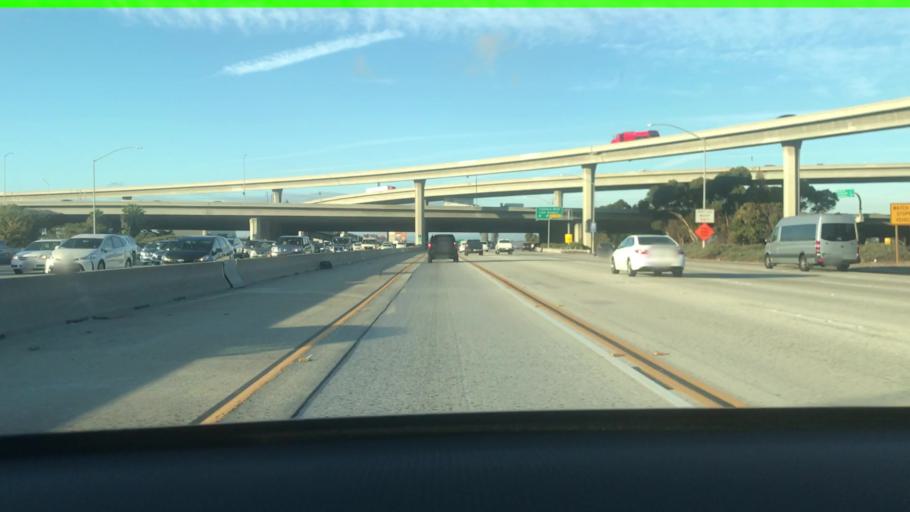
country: US
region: California
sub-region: Los Angeles County
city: Del Aire
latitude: 33.9278
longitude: -118.3683
